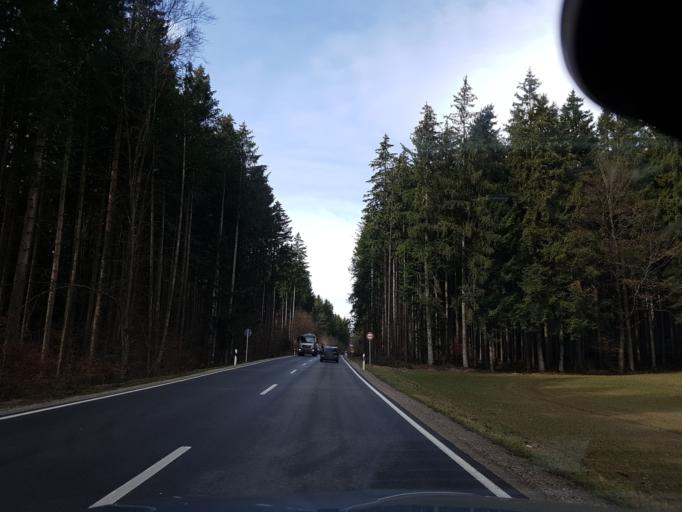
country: DE
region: Bavaria
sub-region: Upper Bavaria
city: Vagen
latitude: 47.8965
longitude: 11.8826
